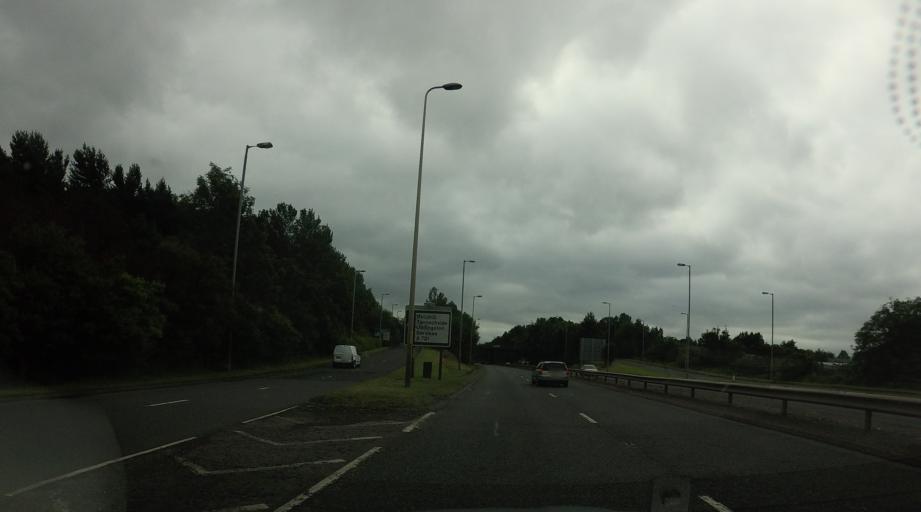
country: GB
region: Scotland
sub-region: North Lanarkshire
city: Bellshill
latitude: 55.8237
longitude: -4.0384
